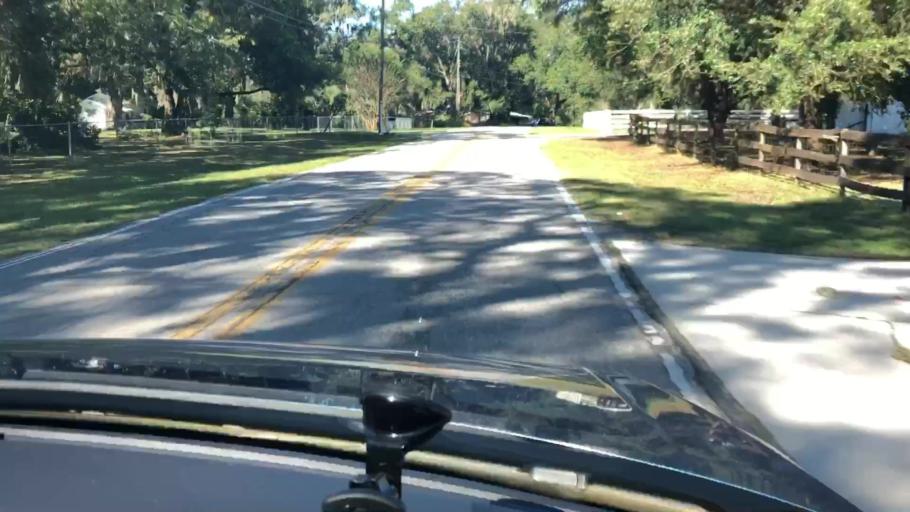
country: US
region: Florida
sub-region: Polk County
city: Kathleen
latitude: 28.1154
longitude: -82.0253
